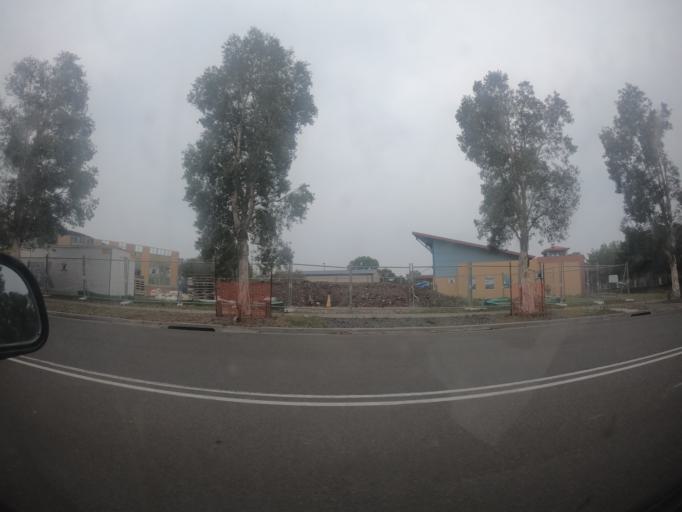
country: AU
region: New South Wales
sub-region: Shellharbour
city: Flinders
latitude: -34.5839
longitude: 150.8487
